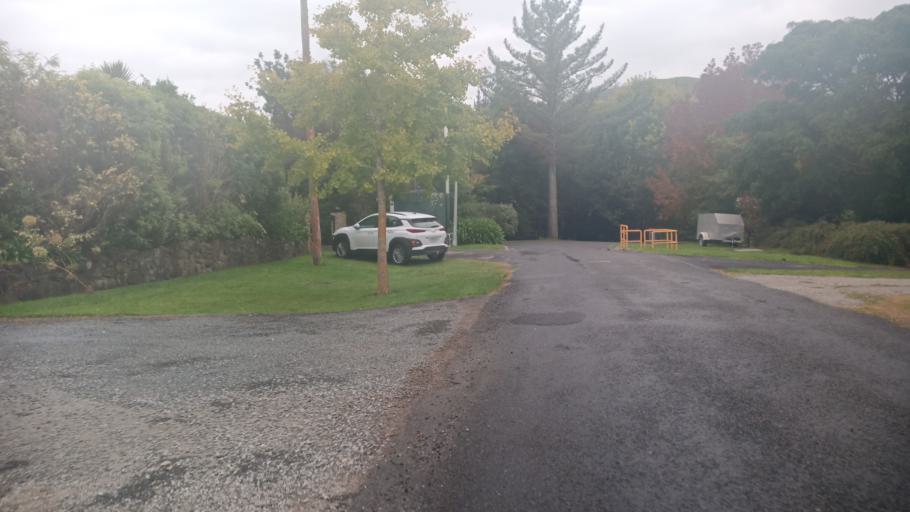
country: NZ
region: Gisborne
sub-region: Gisborne District
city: Gisborne
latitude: -38.6618
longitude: 178.0515
